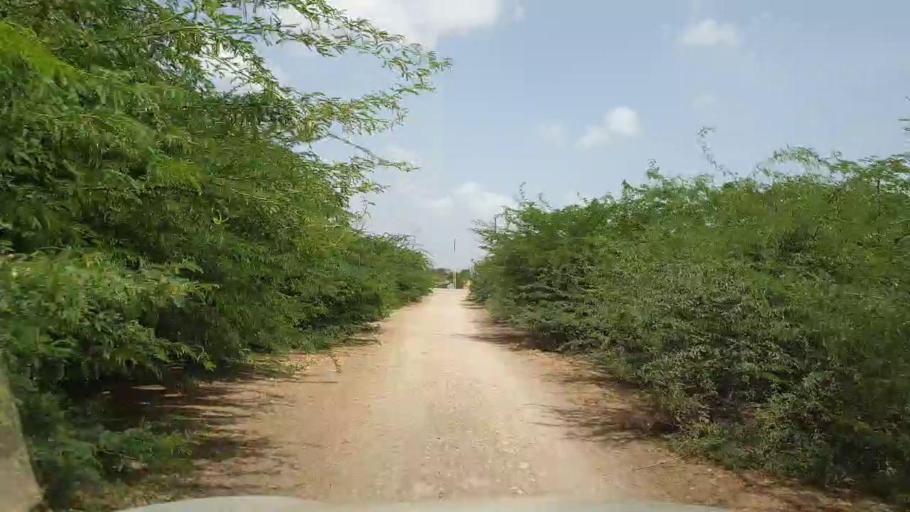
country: PK
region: Sindh
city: Kadhan
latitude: 24.4045
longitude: 68.7983
